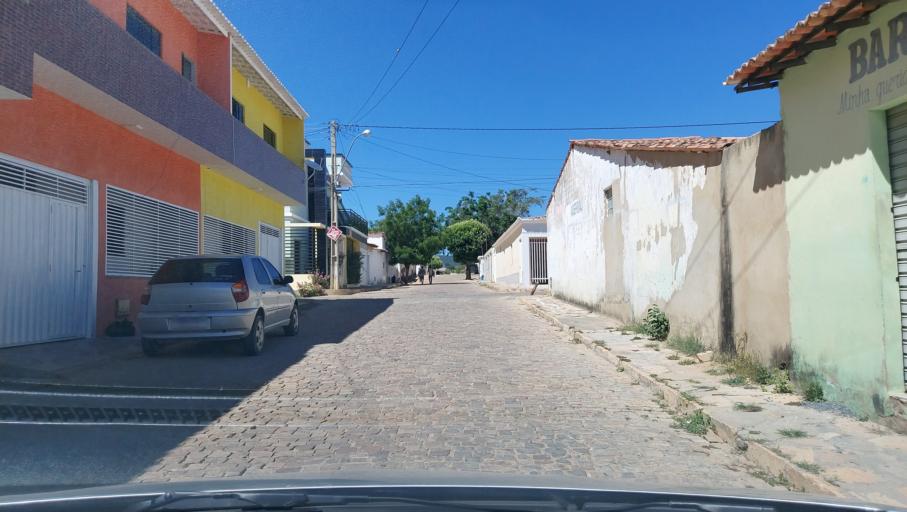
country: BR
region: Bahia
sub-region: Oliveira Dos Brejinhos
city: Beira Rio
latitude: -12.0011
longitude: -42.6278
